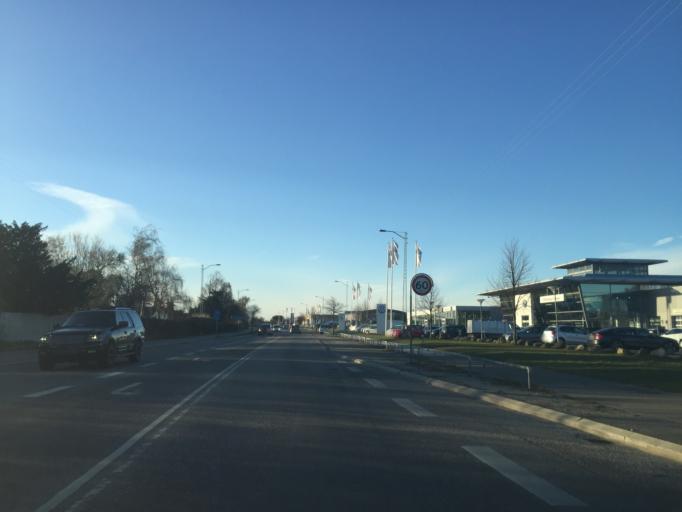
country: DK
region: Capital Region
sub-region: Tarnby Kommune
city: Tarnby
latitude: 55.6128
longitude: 12.6123
